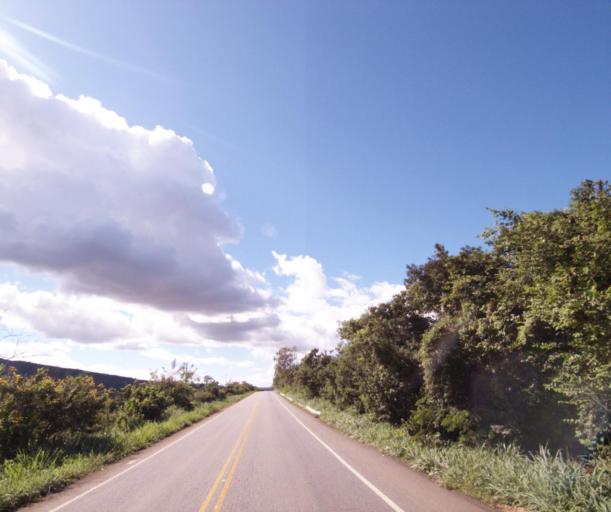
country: BR
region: Bahia
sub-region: Caetite
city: Caetite
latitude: -14.0851
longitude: -42.4502
